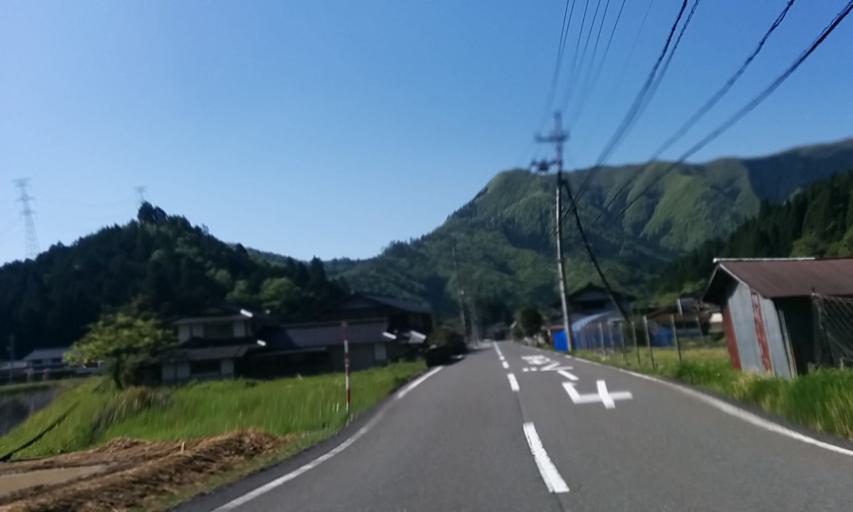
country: JP
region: Kyoto
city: Ayabe
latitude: 35.2597
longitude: 135.4536
